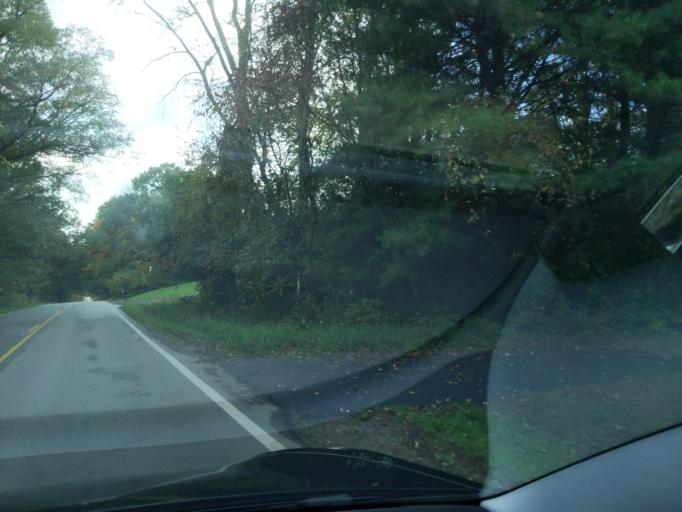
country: US
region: Michigan
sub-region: Ingham County
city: Leslie
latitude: 42.3713
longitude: -84.4478
